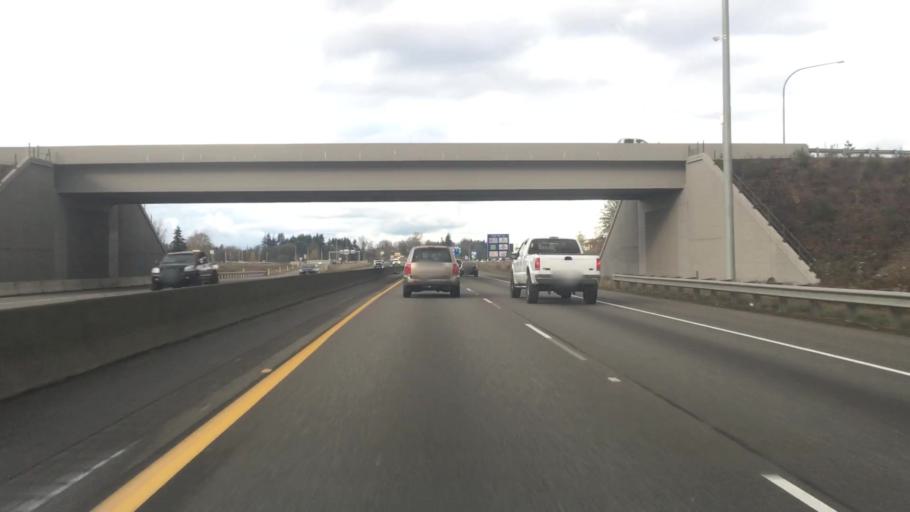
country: US
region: Washington
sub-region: Lewis County
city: Centralia
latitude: 46.7064
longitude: -122.9738
